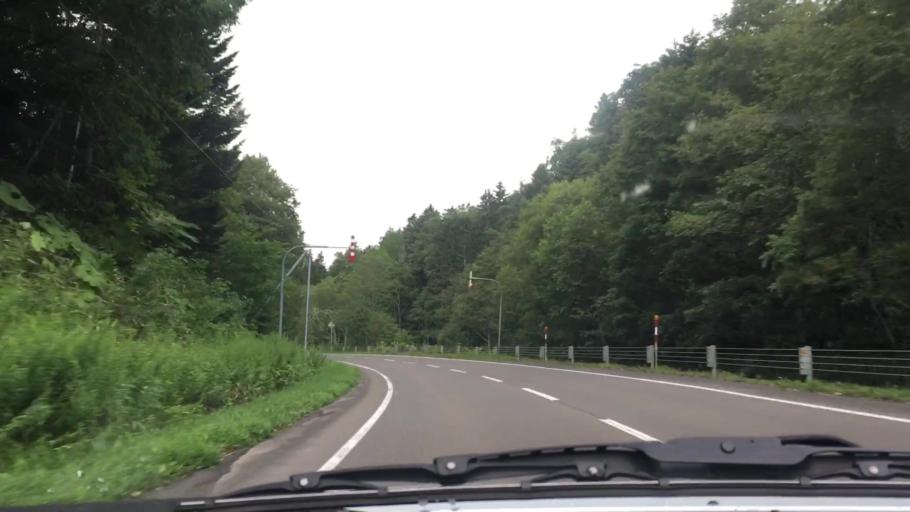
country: JP
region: Hokkaido
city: Shimo-furano
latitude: 43.0688
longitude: 142.6690
